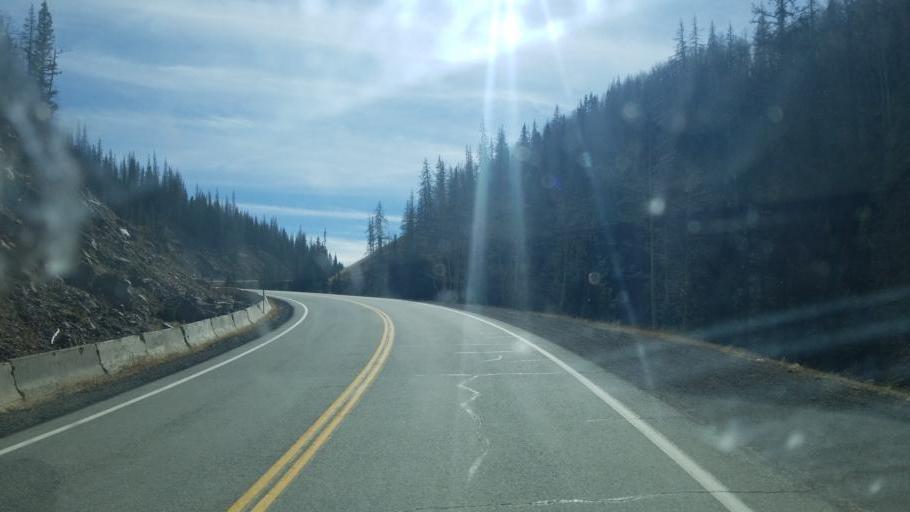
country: US
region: New Mexico
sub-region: Rio Arriba County
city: Chama
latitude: 37.1020
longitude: -106.3750
